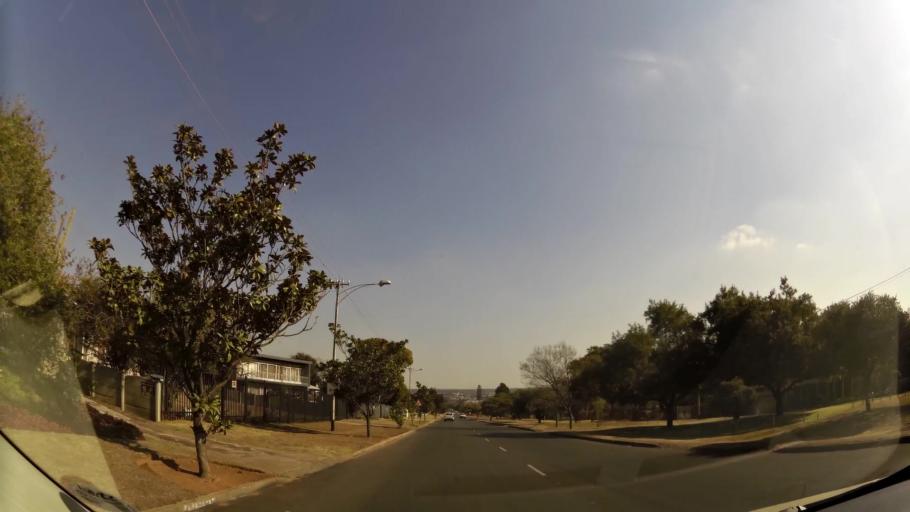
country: ZA
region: Gauteng
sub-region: West Rand District Municipality
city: Randfontein
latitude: -26.1571
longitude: 27.6965
